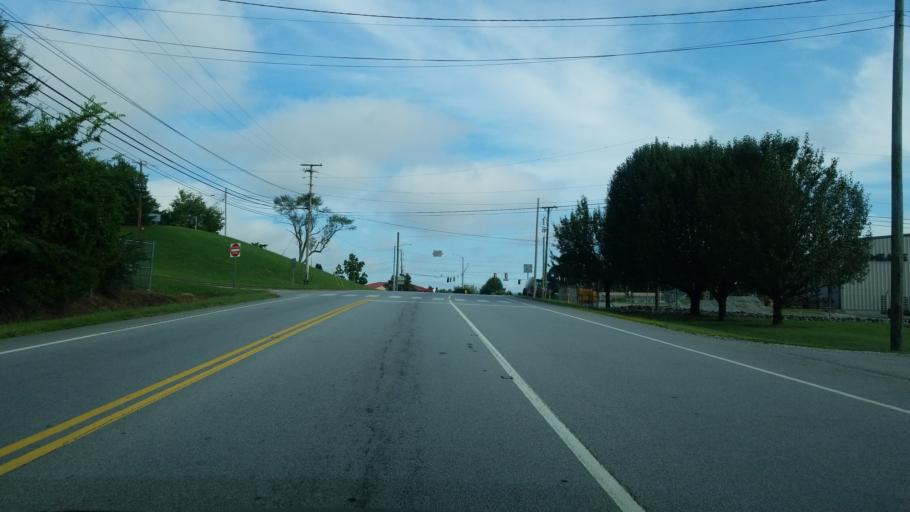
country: US
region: Tennessee
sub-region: Hamilton County
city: East Chattanooga
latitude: 35.0801
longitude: -85.2088
